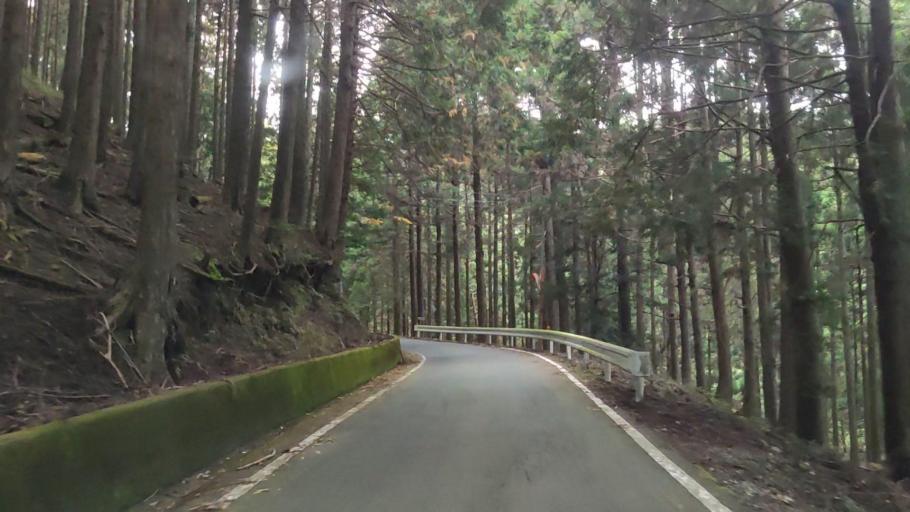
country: JP
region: Shizuoka
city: Ito
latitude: 34.8986
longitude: 138.9598
